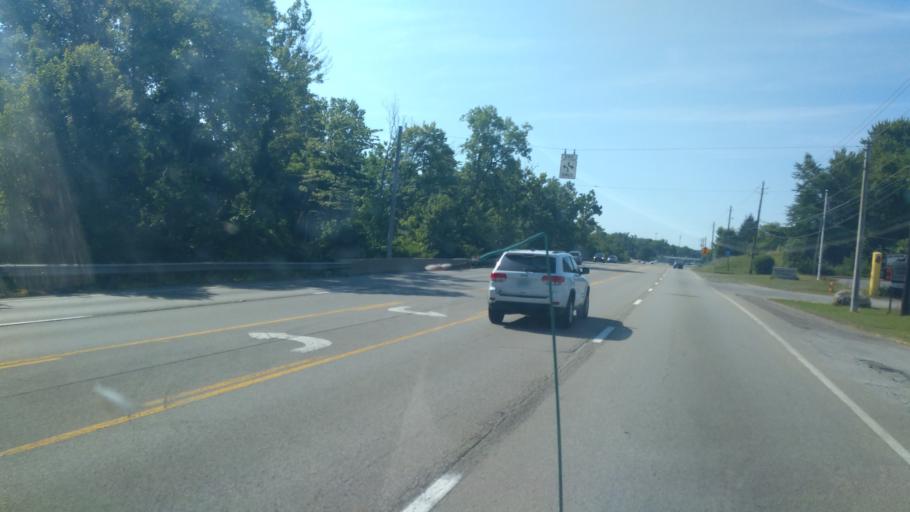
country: US
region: Ohio
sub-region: Delaware County
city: Delaware
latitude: 40.3187
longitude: -83.0692
